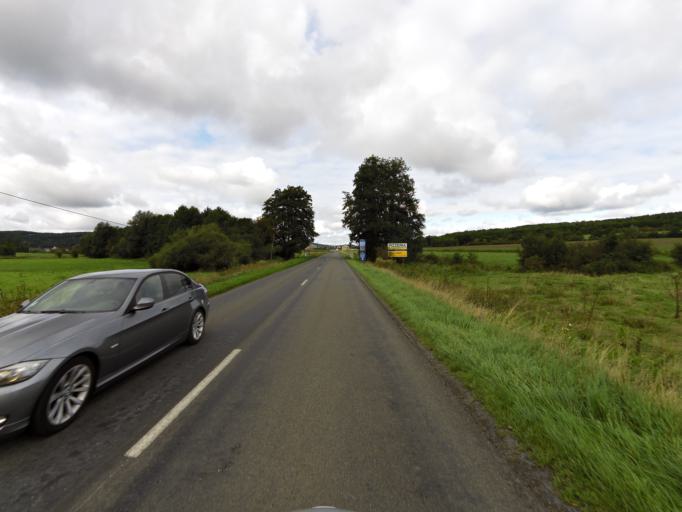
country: FR
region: Champagne-Ardenne
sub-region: Departement des Ardennes
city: Fromelennes
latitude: 50.1311
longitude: 4.8721
